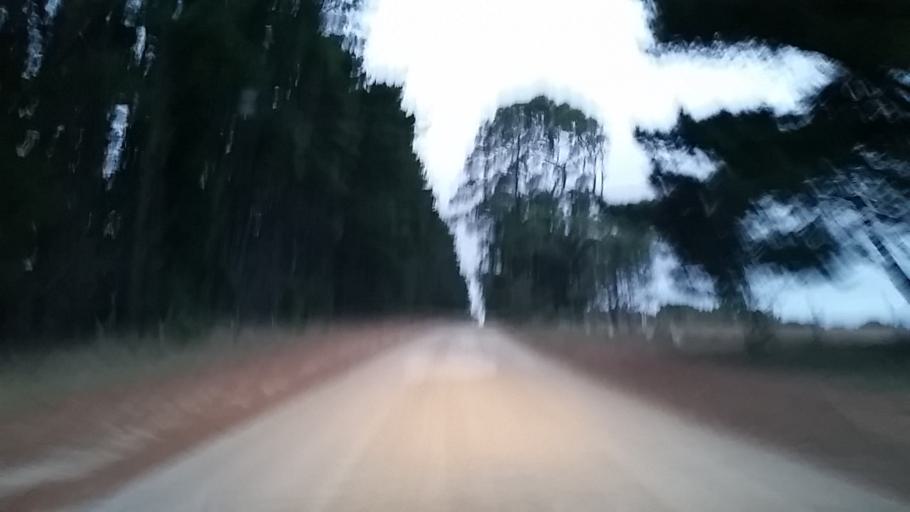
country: AU
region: South Australia
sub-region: Yankalilla
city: Normanville
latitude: -35.6098
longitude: 138.1887
